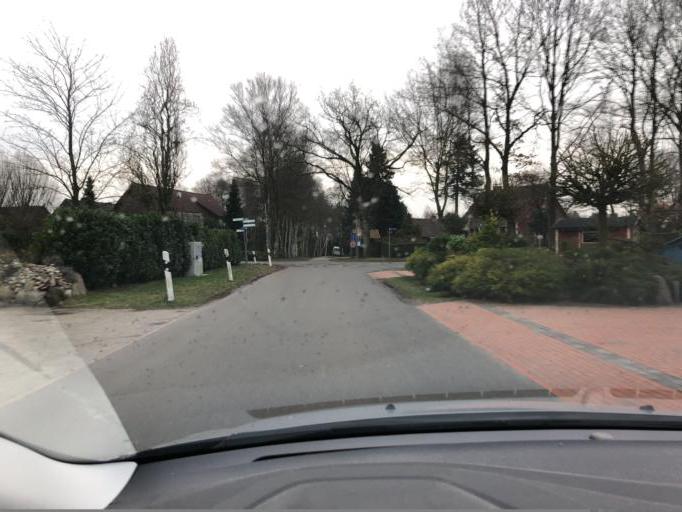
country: DE
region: Lower Saxony
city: Bad Zwischenahn
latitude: 53.1650
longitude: 8.0384
